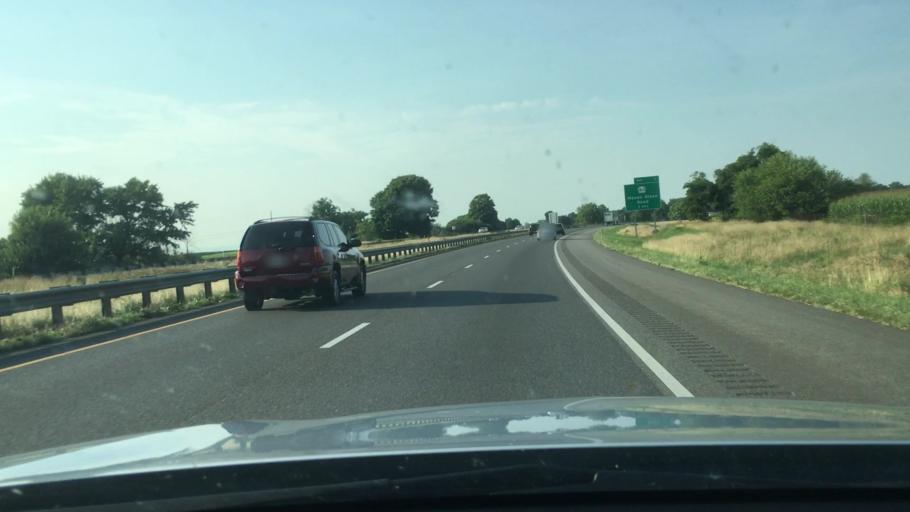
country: US
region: Maryland
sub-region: Washington County
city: Maugansville
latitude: 39.7091
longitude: -77.7427
